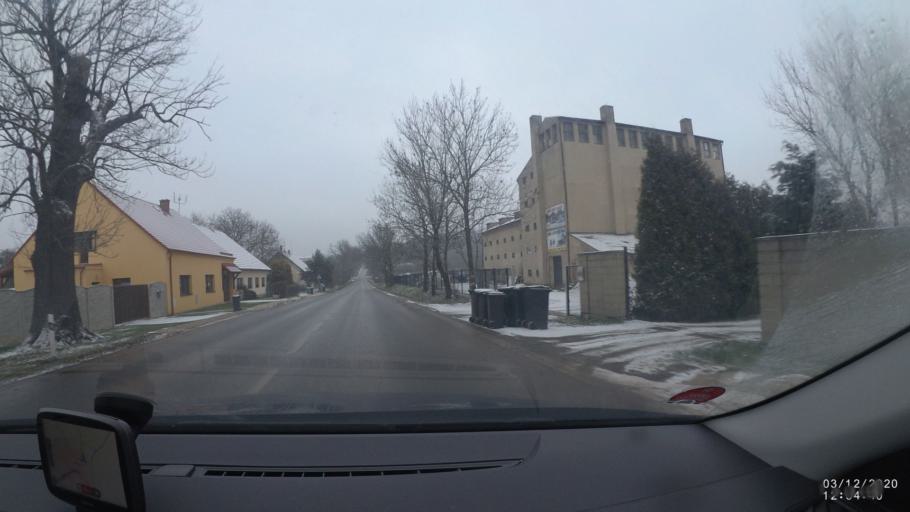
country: CZ
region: Central Bohemia
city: Revnicov
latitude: 50.1873
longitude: 13.8122
